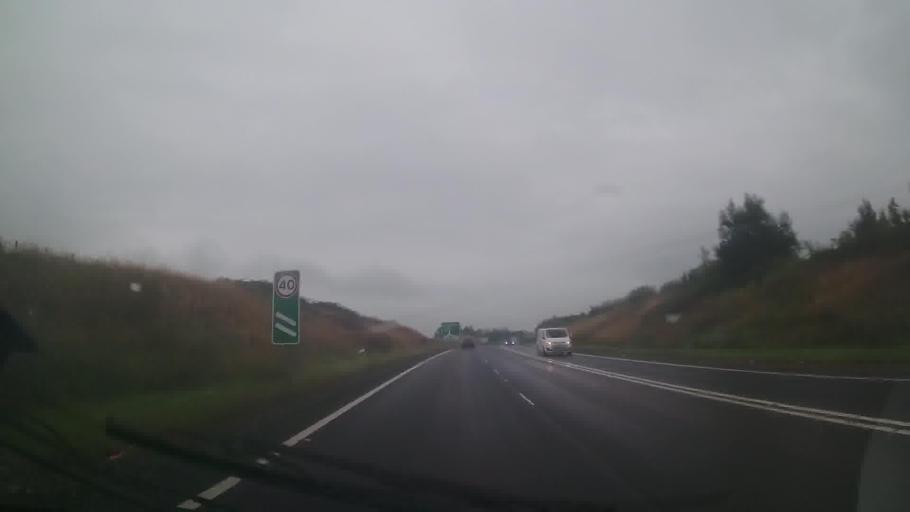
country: GB
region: Scotland
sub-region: North Ayrshire
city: Ardrossan
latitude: 55.6604
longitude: -4.8134
